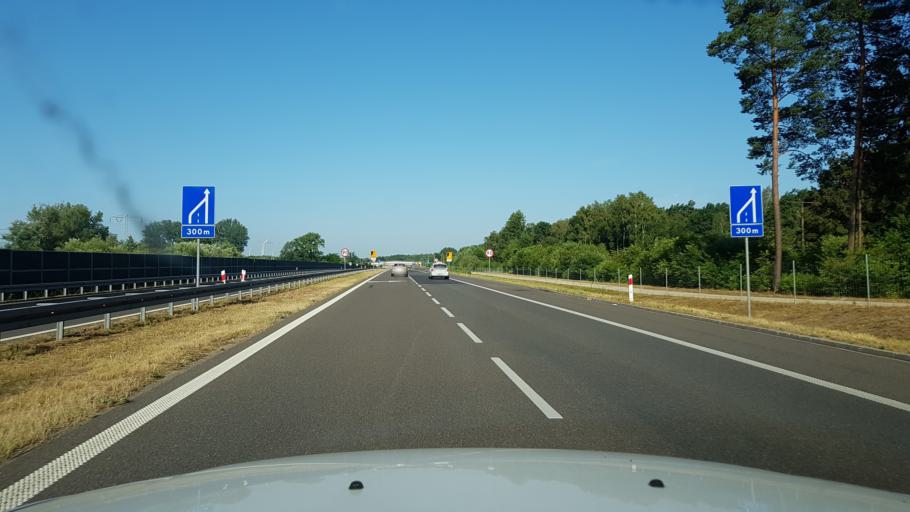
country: PL
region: West Pomeranian Voivodeship
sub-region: Powiat goleniowski
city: Przybiernow
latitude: 53.8422
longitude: 14.7268
